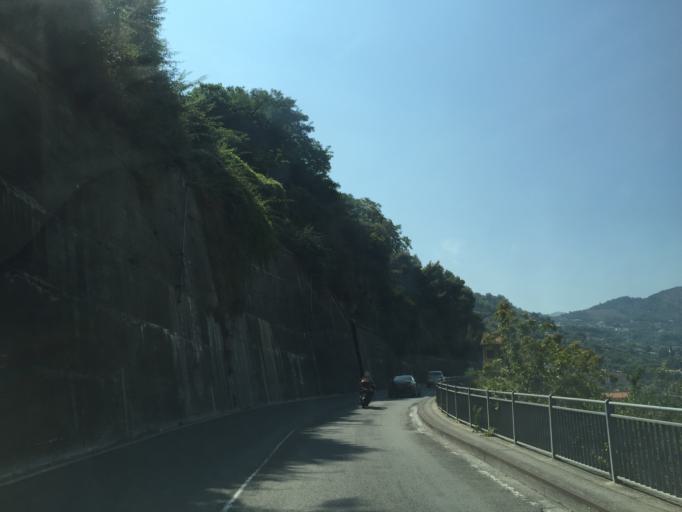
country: IT
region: Liguria
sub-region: Provincia di Imperia
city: Ventimiglia
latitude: 43.7936
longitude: 7.5991
